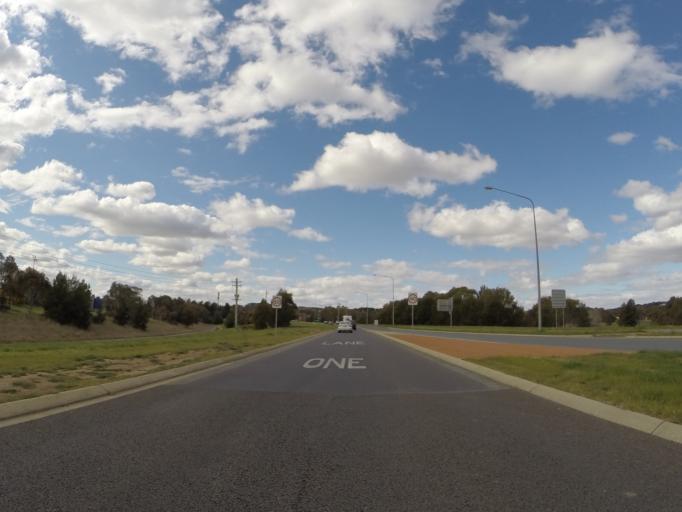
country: AU
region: Australian Capital Territory
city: Belconnen
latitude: -35.2158
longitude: 149.0849
